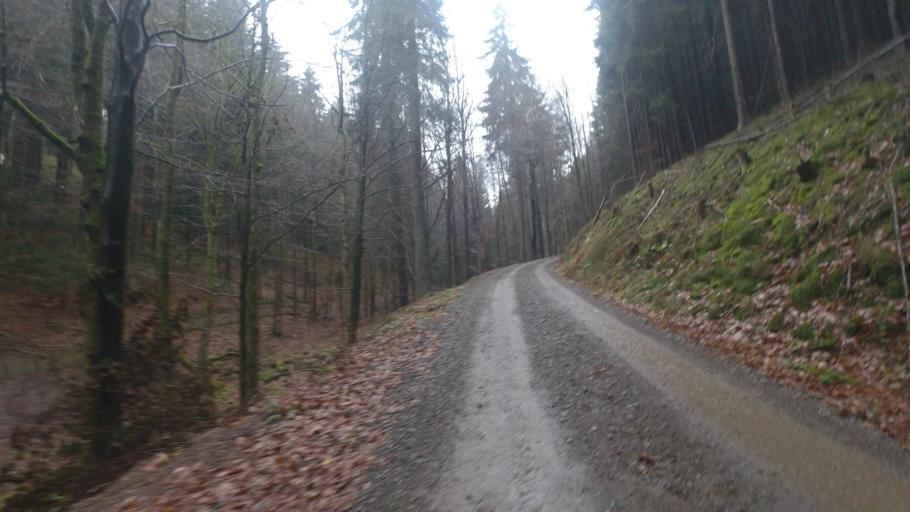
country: DE
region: Thuringia
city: Frankenhain
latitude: 50.7193
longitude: 10.7749
